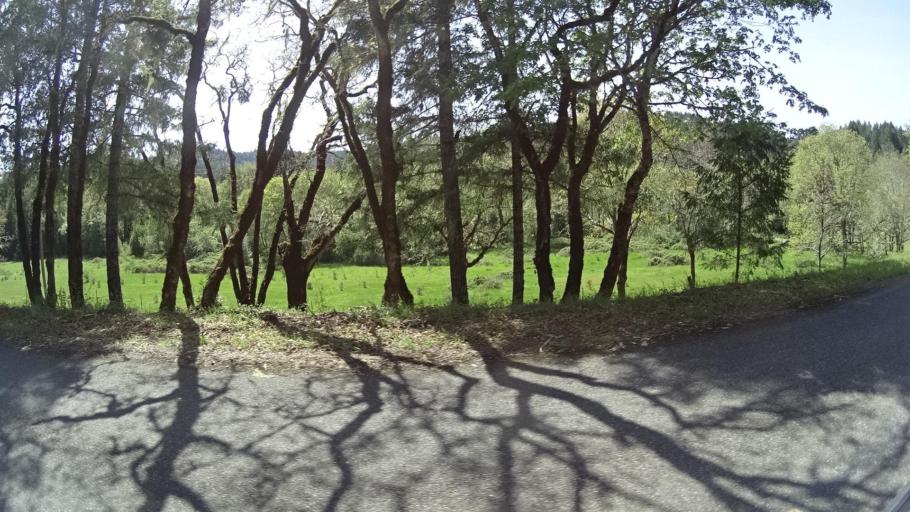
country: US
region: California
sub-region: Humboldt County
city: Redway
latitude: 40.3001
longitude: -123.6538
